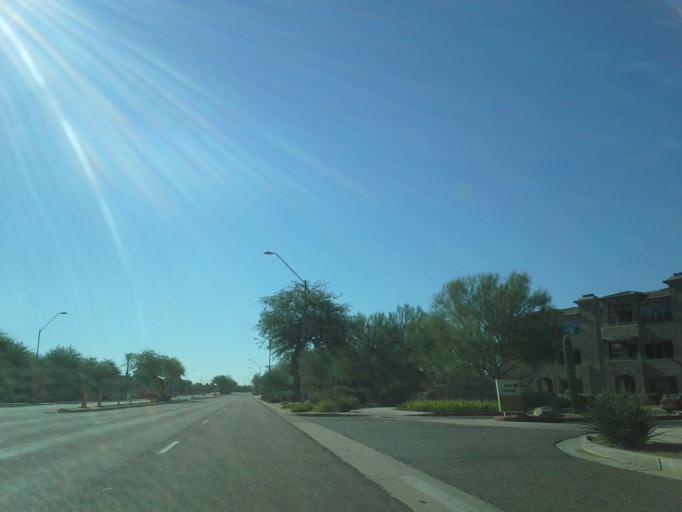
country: US
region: Arizona
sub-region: Maricopa County
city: Paradise Valley
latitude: 33.6182
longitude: -111.8725
